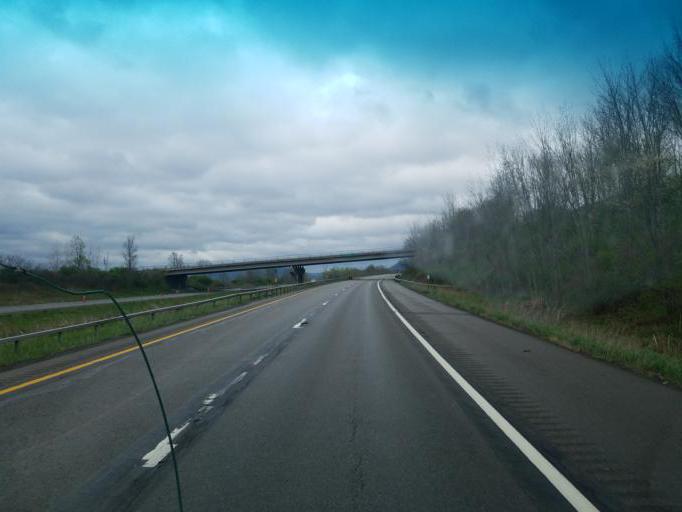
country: US
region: New York
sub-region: Cattaraugus County
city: Randolph
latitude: 42.1479
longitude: -78.9678
